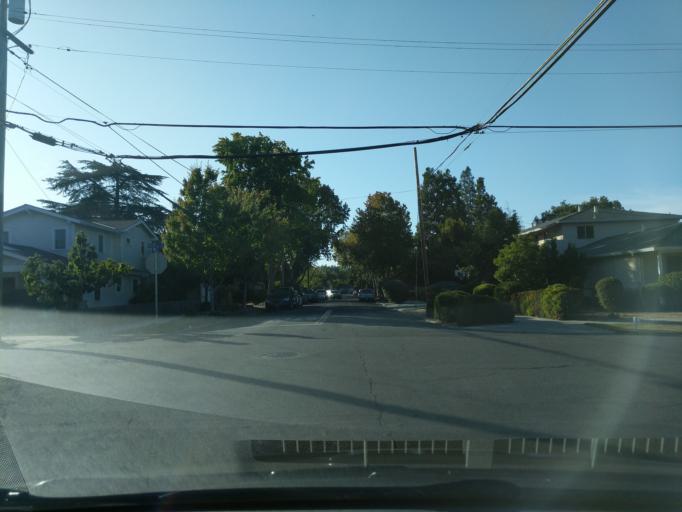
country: US
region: California
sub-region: Santa Clara County
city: Mountain View
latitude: 37.3931
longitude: -122.0890
